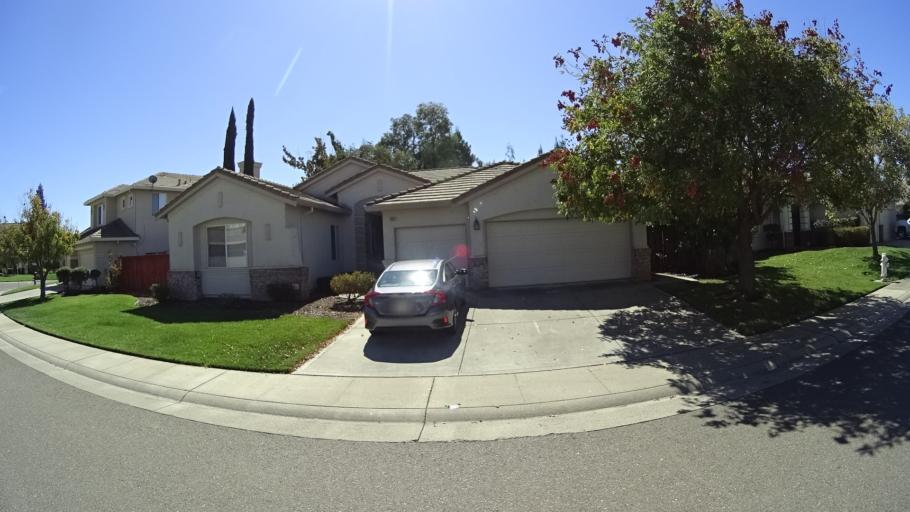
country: US
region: California
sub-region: Sacramento County
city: Laguna
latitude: 38.4156
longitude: -121.4660
